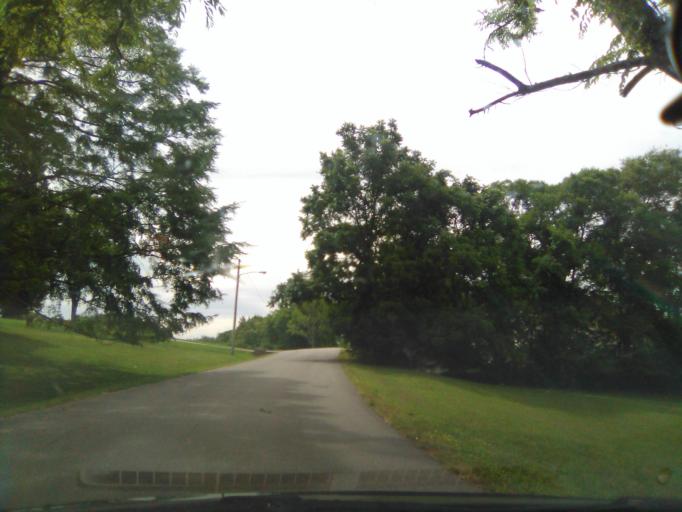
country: US
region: Tennessee
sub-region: Davidson County
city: Belle Meade
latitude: 36.0992
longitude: -86.8873
